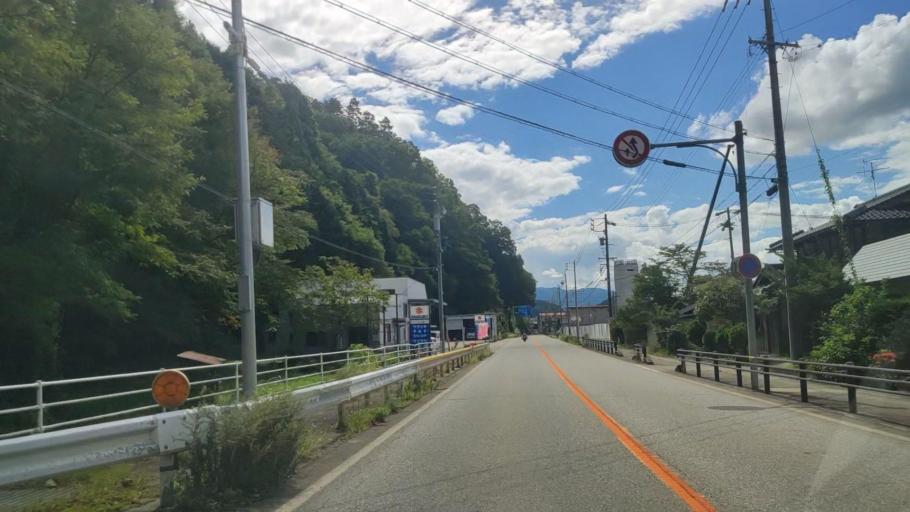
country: JP
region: Gifu
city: Takayama
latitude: 36.1746
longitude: 137.2486
